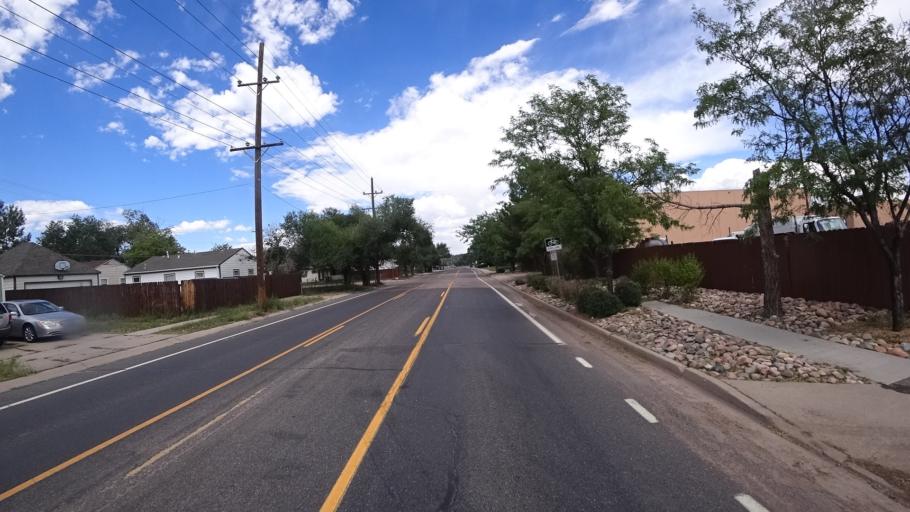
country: US
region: Colorado
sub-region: El Paso County
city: Stratmoor
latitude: 38.8006
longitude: -104.8035
